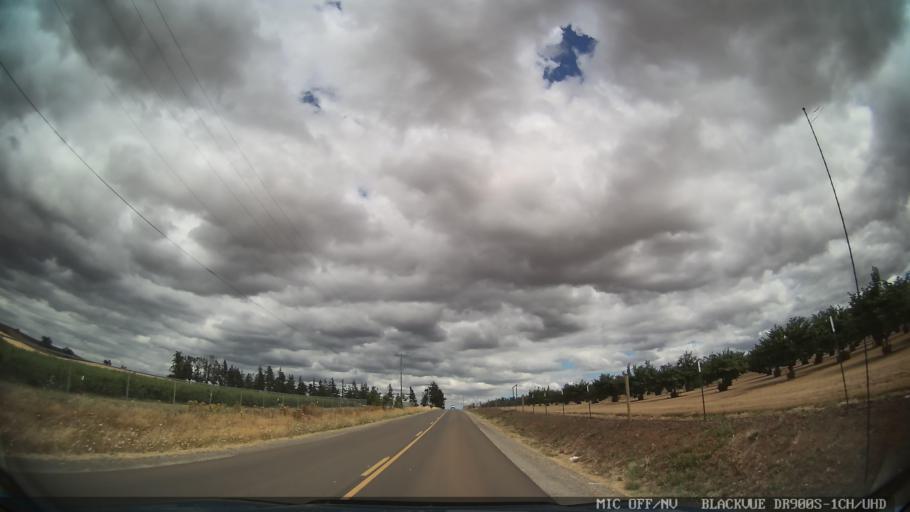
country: US
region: Oregon
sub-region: Marion County
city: Sublimity
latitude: 44.8661
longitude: -122.7694
